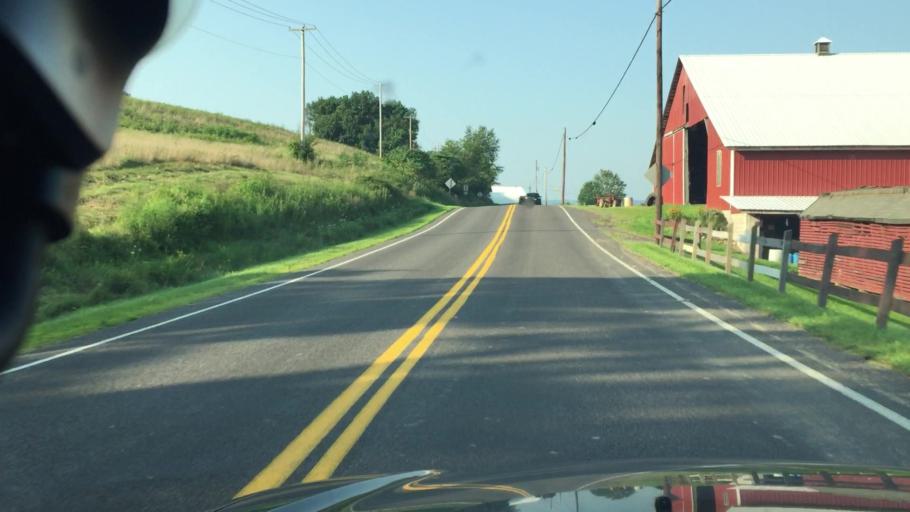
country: US
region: Pennsylvania
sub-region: Columbia County
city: Mifflinville
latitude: 41.0004
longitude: -76.3240
